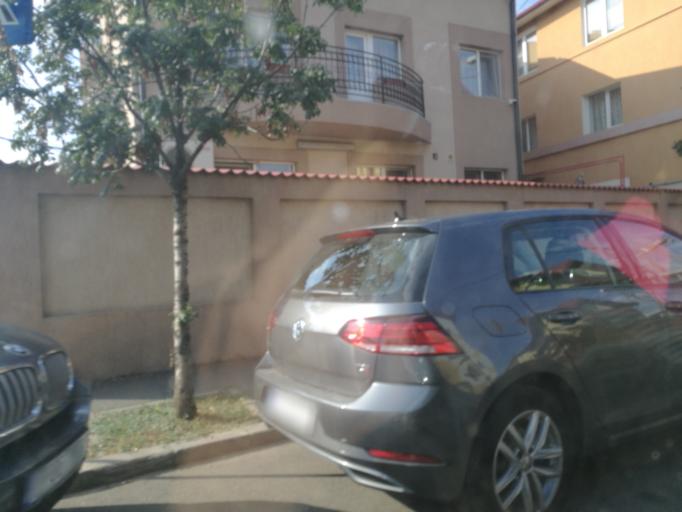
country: RO
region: Ilfov
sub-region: Comuna Chiajna
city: Rosu
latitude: 44.4728
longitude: 26.0536
